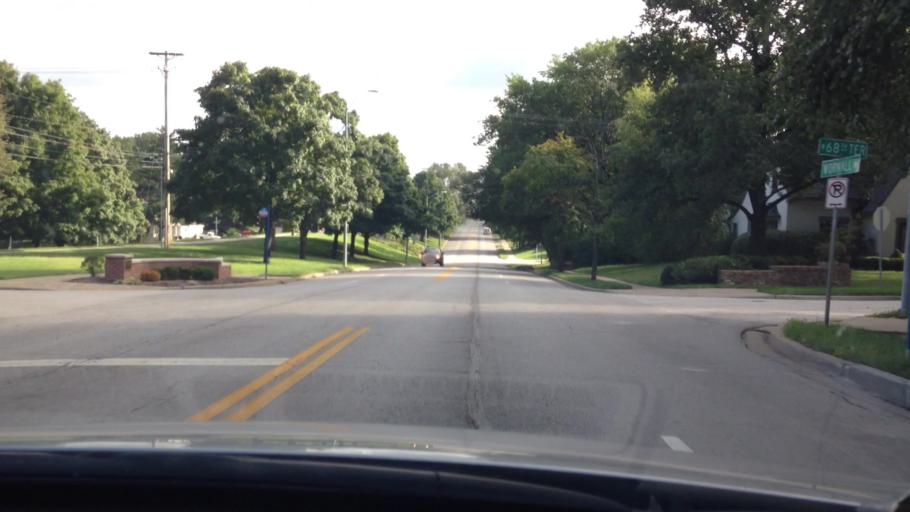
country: US
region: Kansas
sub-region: Johnson County
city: Mission Hills
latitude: 39.0051
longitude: -94.5934
